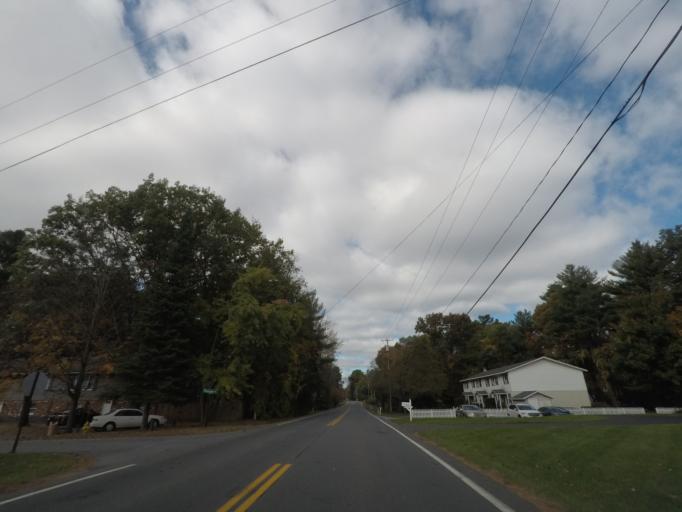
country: US
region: New York
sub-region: Albany County
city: Cohoes
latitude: 42.8327
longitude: -73.7586
